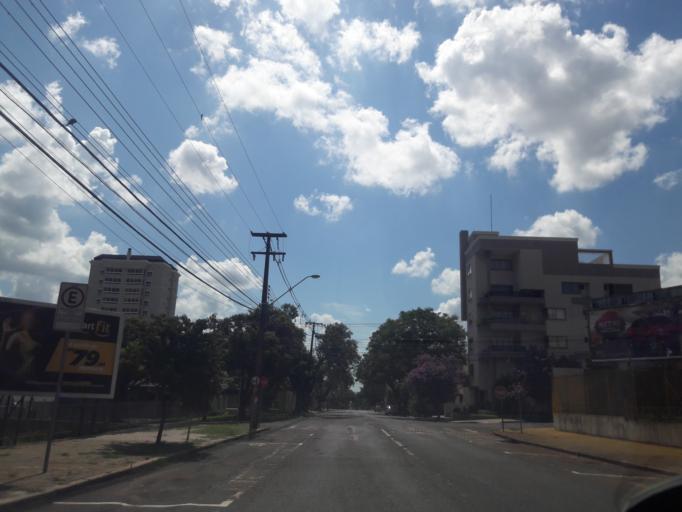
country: BR
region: Parana
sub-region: Cascavel
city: Cascavel
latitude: -24.9601
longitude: -53.4603
